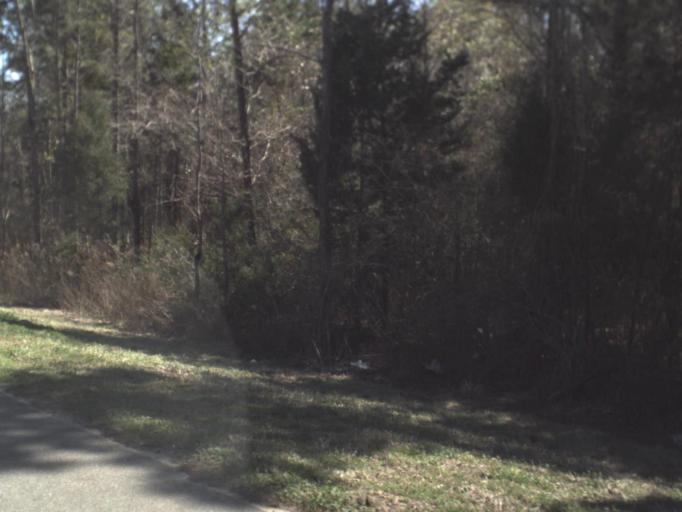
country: US
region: Florida
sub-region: Jackson County
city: Marianna
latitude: 30.8056
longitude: -85.2855
